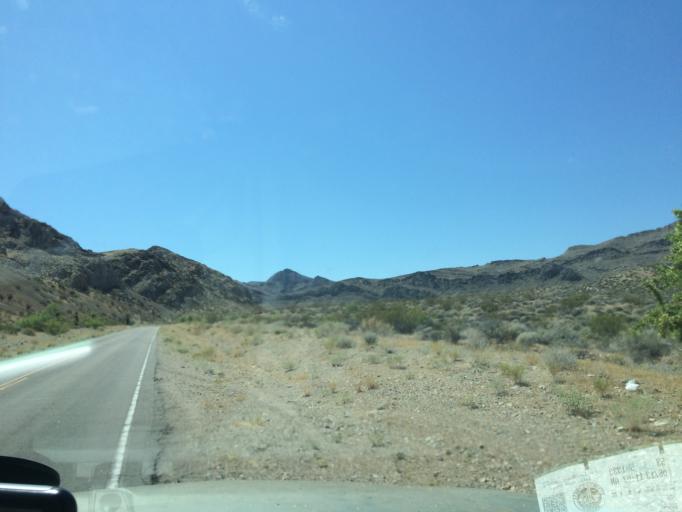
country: US
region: Nevada
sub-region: Clark County
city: Moapa Valley
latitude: 36.4259
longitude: -114.6246
